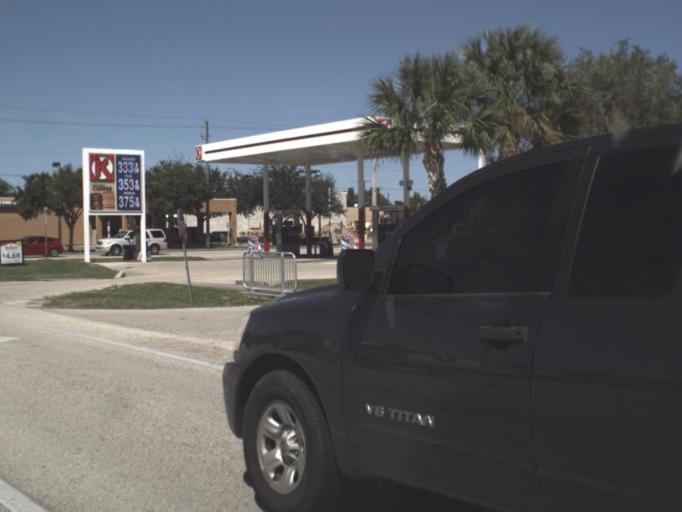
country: US
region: Florida
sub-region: Lee County
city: San Carlos Park
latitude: 26.4627
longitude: -81.8297
